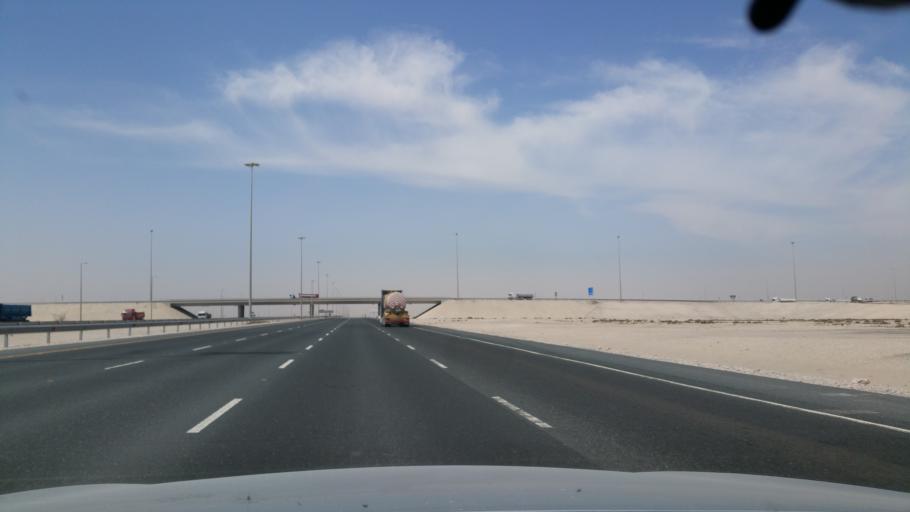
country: QA
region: Baladiyat ar Rayyan
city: Ash Shahaniyah
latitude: 25.1106
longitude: 51.1703
